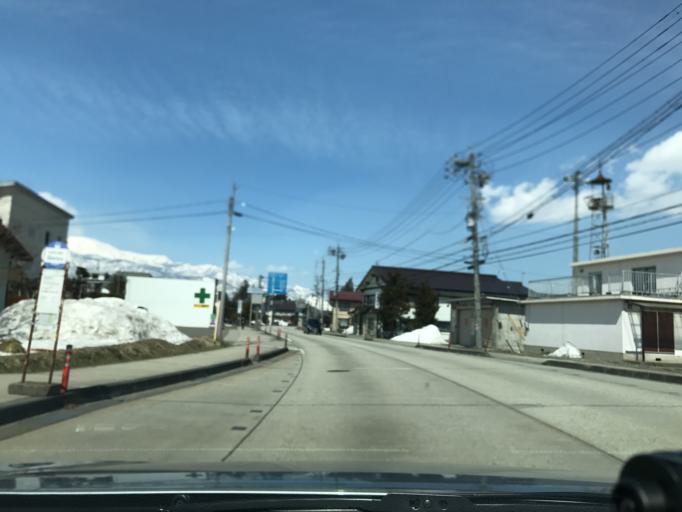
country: JP
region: Nagano
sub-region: Kitaazumi Gun
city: Hakuba
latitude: 36.6568
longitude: 137.8480
